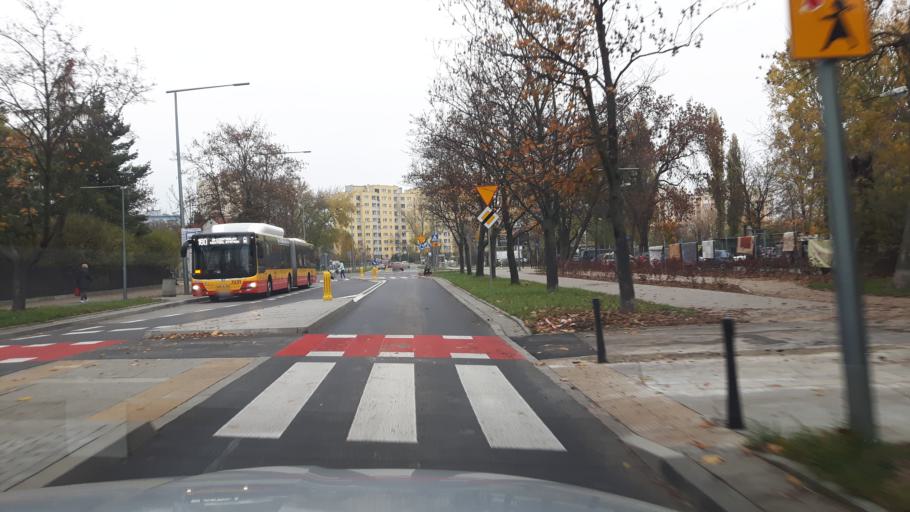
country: PL
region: Masovian Voivodeship
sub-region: Warszawa
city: Targowek
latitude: 52.2722
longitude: 21.0461
